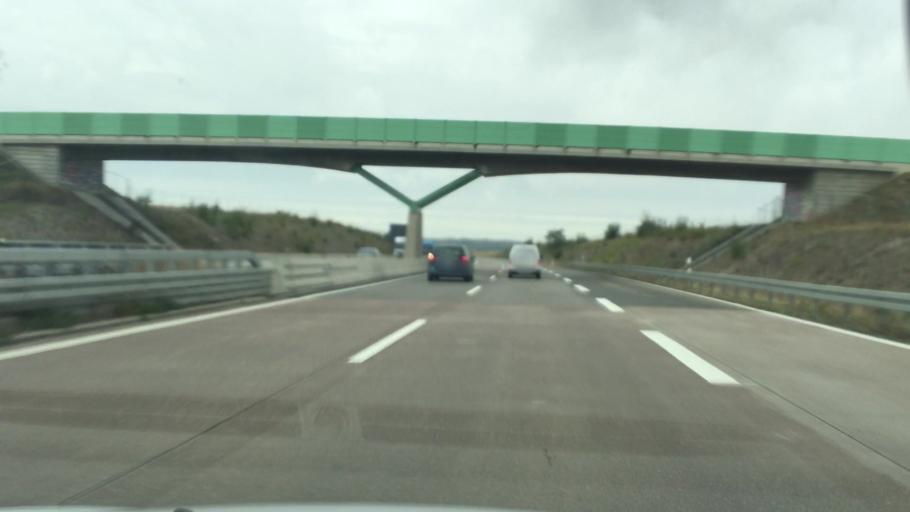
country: DE
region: Saxony
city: Narsdorf
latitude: 50.9986
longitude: 12.6907
